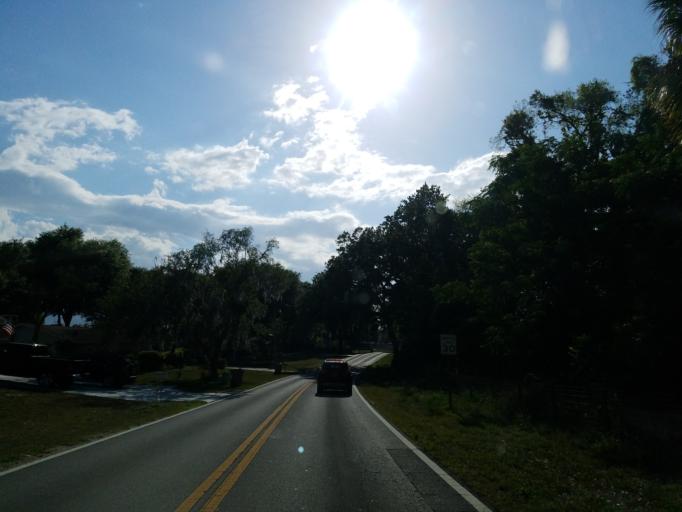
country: US
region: Florida
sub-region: Lake County
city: Fruitland Park
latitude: 28.8497
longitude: -81.8951
